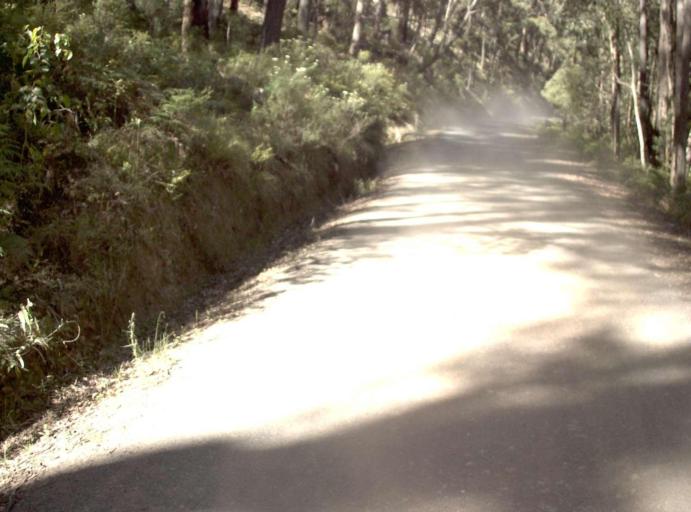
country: AU
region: New South Wales
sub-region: Bombala
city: Bombala
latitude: -37.2591
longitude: 148.7331
